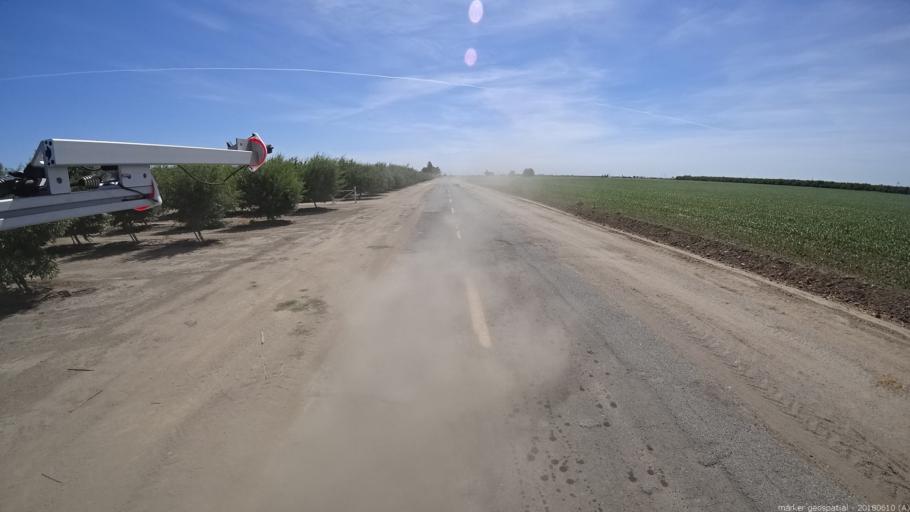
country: US
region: California
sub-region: Madera County
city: Chowchilla
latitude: 37.0253
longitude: -120.3628
